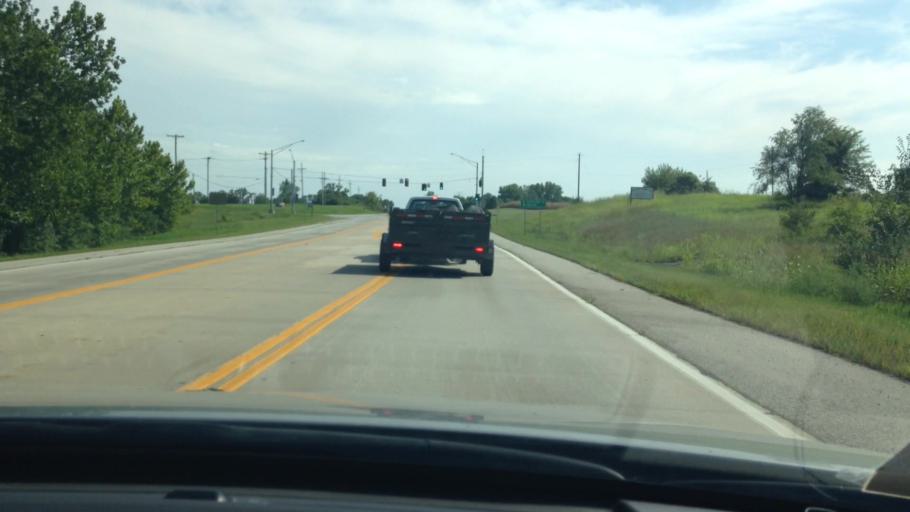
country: US
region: Missouri
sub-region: Cass County
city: Belton
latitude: 38.8194
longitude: -94.5857
